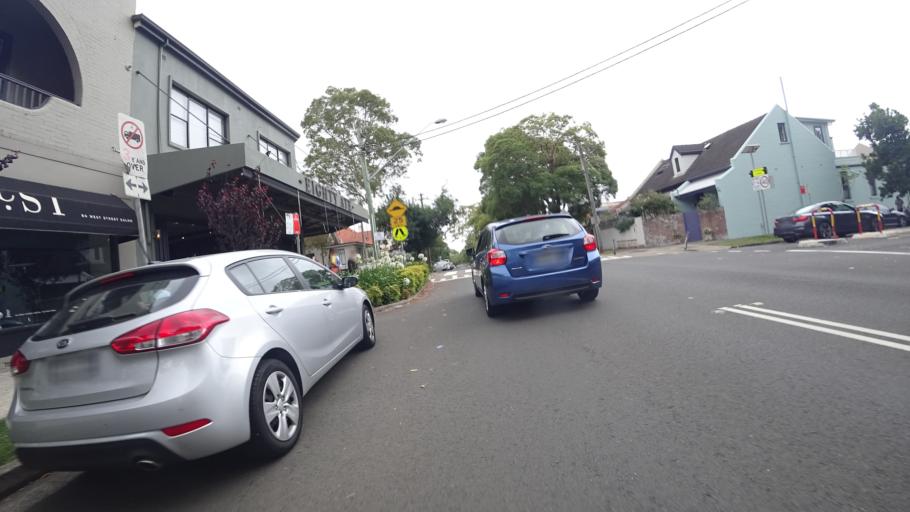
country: AU
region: New South Wales
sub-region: North Sydney
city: Crows Nest
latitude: -33.8306
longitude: 151.2059
